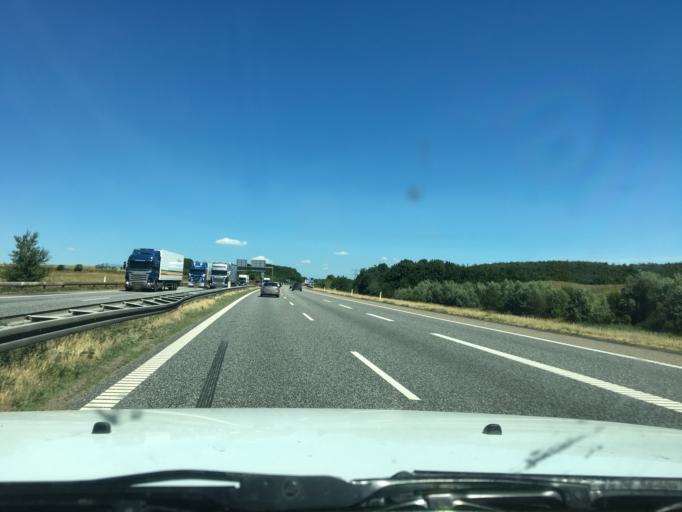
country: DK
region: Central Jutland
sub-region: Arhus Kommune
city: Framlev
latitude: 56.1637
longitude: 10.0480
